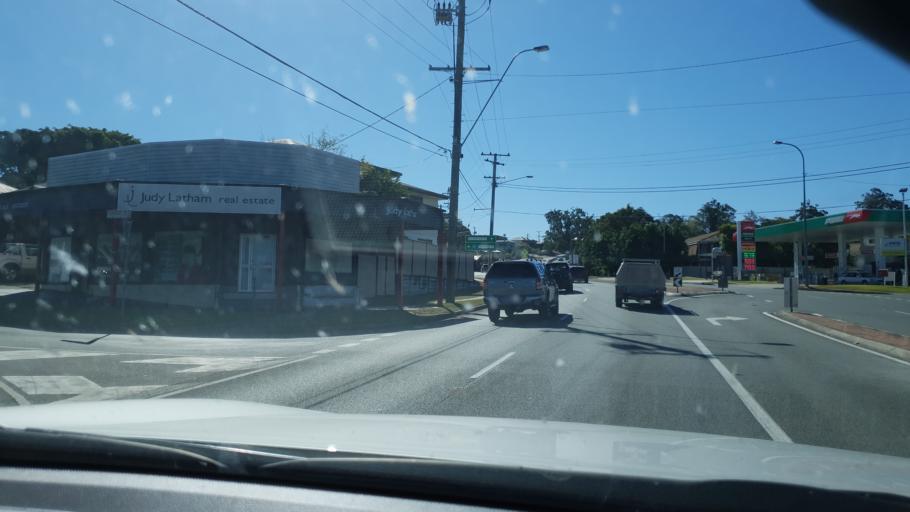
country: AU
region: Queensland
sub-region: Brisbane
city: Everton Park
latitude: -27.4020
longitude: 152.9869
